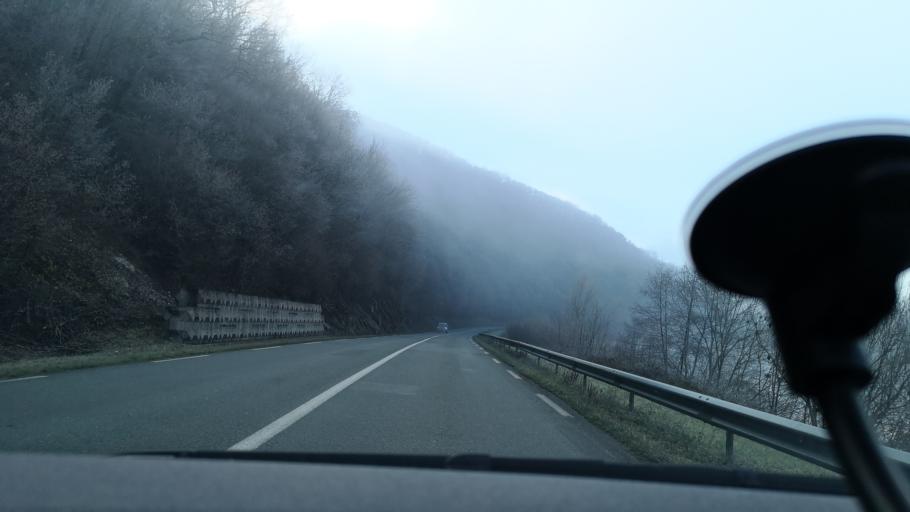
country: FR
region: Franche-Comte
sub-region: Departement du Doubs
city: Clerval
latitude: 47.3998
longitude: 6.5096
